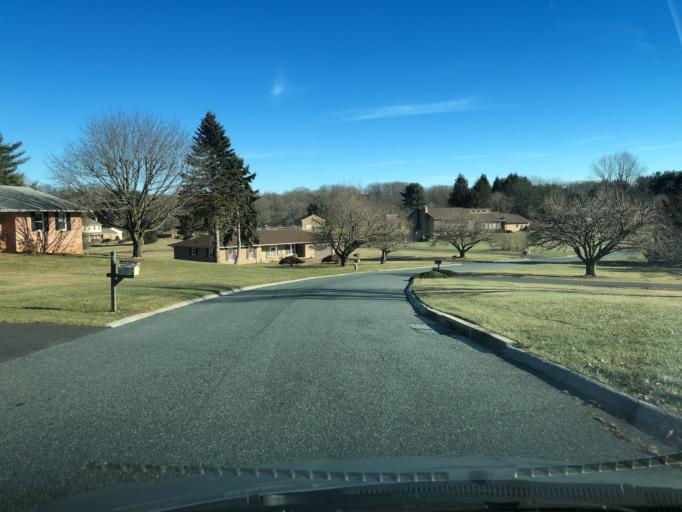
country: US
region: Maryland
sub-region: Baltimore County
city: Kingsville
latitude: 39.4622
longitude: -76.4488
